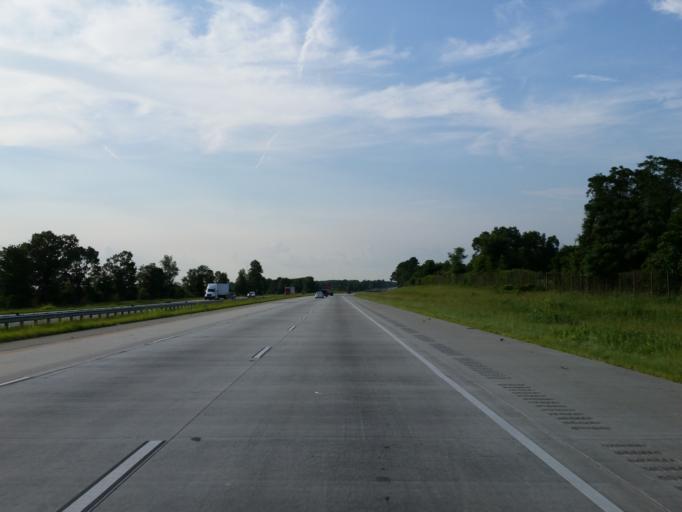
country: US
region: Georgia
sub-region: Dooly County
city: Unadilla
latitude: 32.2921
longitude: -83.7594
